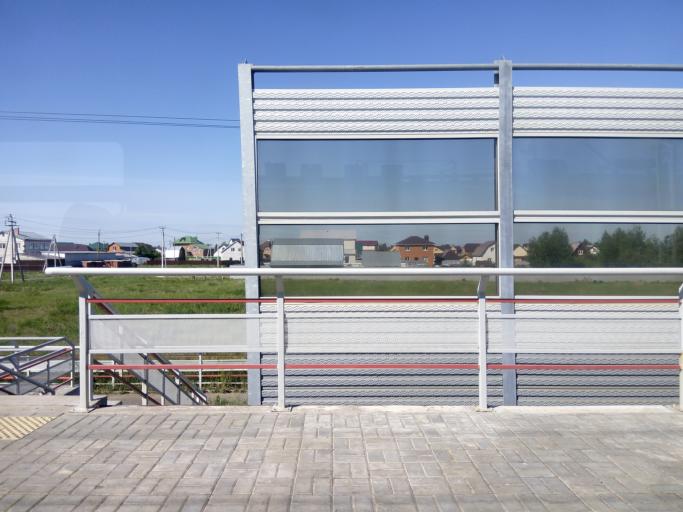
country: RU
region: Tatarstan
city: Stolbishchi
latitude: 55.6523
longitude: 49.2309
